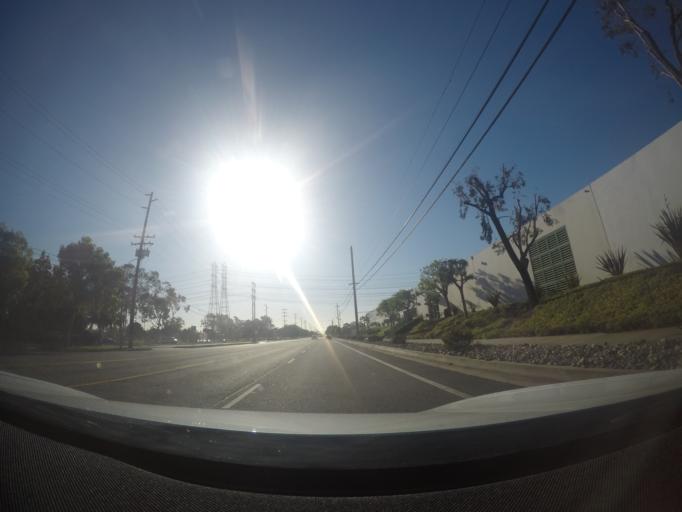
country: US
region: California
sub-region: Los Angeles County
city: Torrance
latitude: 33.8582
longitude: -118.3485
